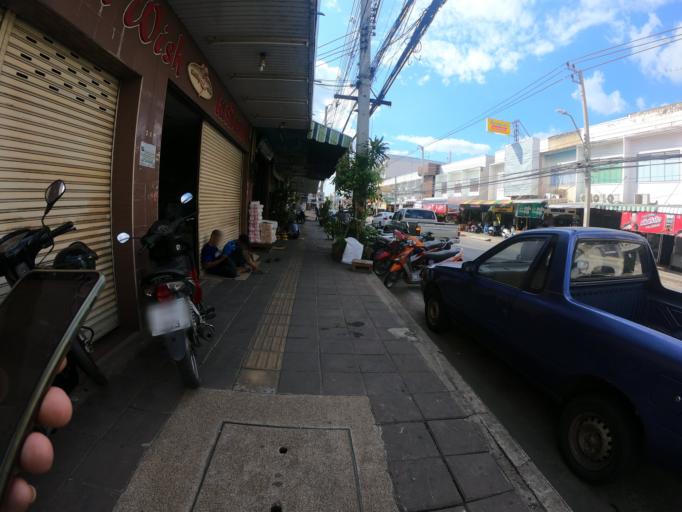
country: TH
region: Nakhon Ratchasima
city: Nakhon Ratchasima
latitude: 14.9766
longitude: 102.0940
